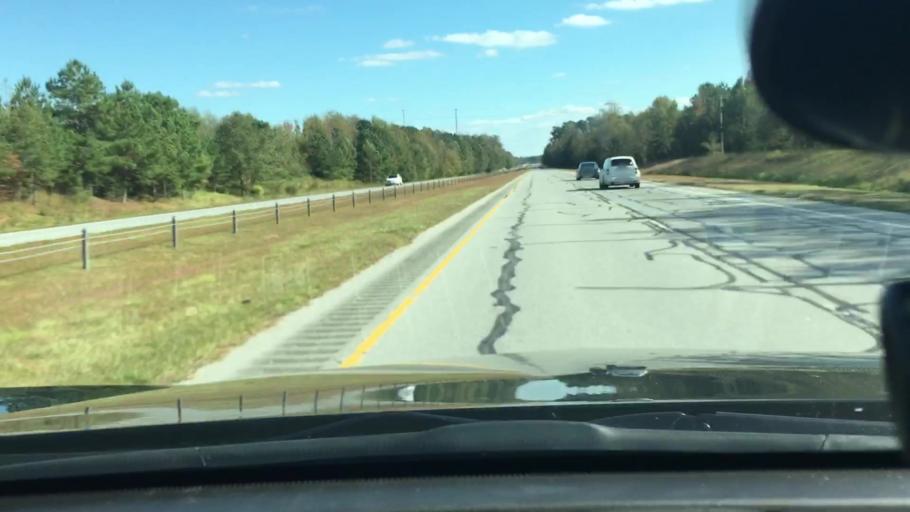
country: US
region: North Carolina
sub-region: Pitt County
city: Farmville
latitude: 35.6165
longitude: -77.5861
